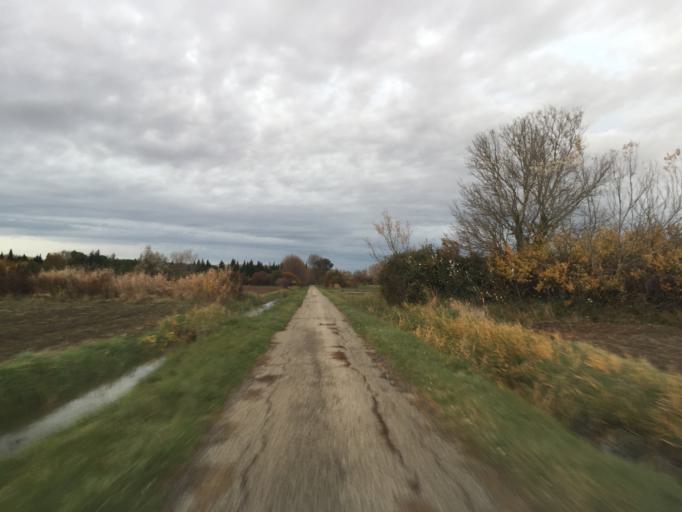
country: FR
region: Provence-Alpes-Cote d'Azur
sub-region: Departement du Vaucluse
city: Courthezon
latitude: 44.0839
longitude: 4.8685
